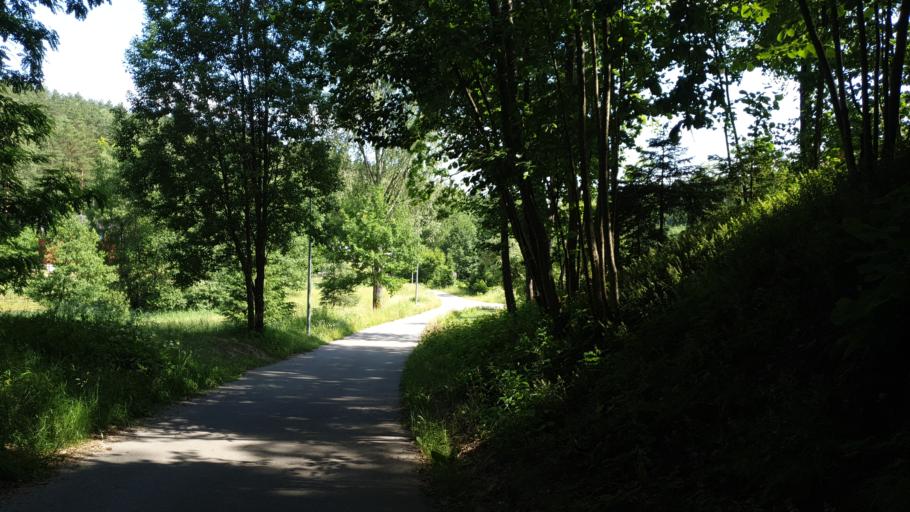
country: LT
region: Vilnius County
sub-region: Vilnius
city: Fabijoniskes
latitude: 54.7849
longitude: 25.3257
